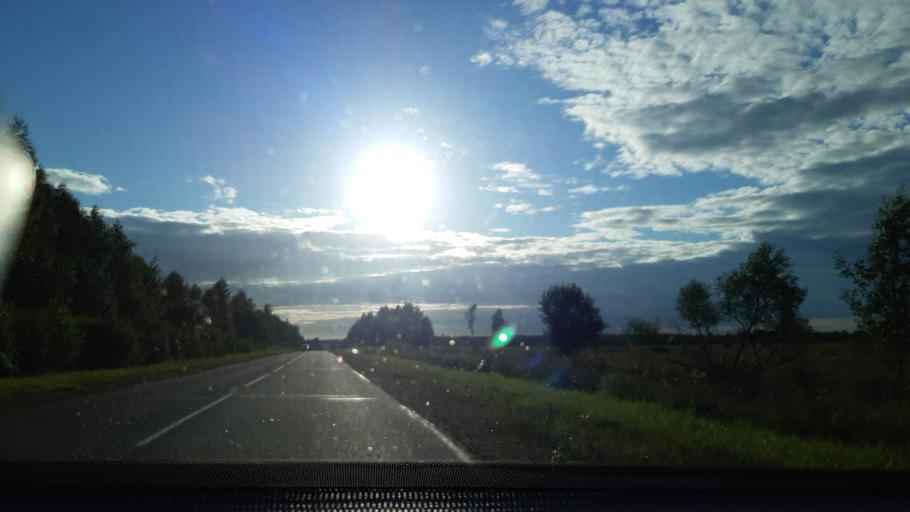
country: RU
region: Smolensk
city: Yel'nya
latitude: 54.5585
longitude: 33.1800
